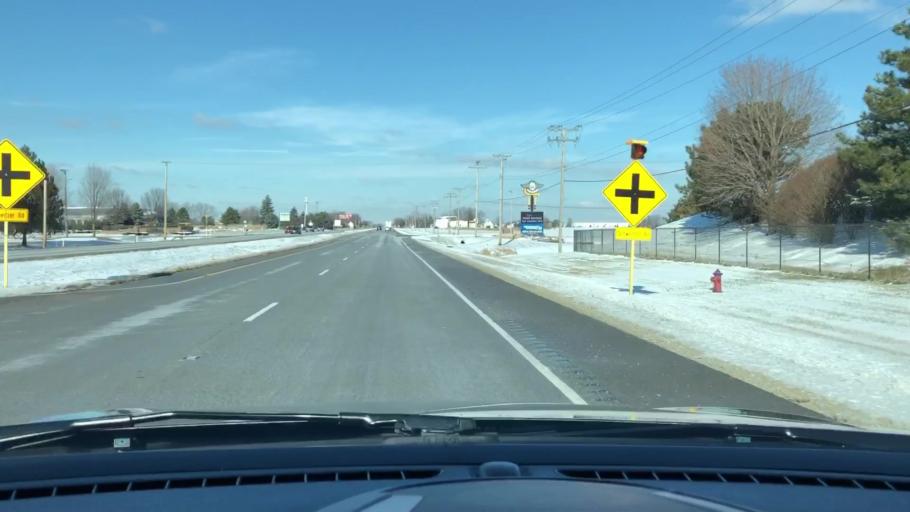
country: US
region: Illinois
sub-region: Will County
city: Preston Heights
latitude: 41.4653
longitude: -88.0792
